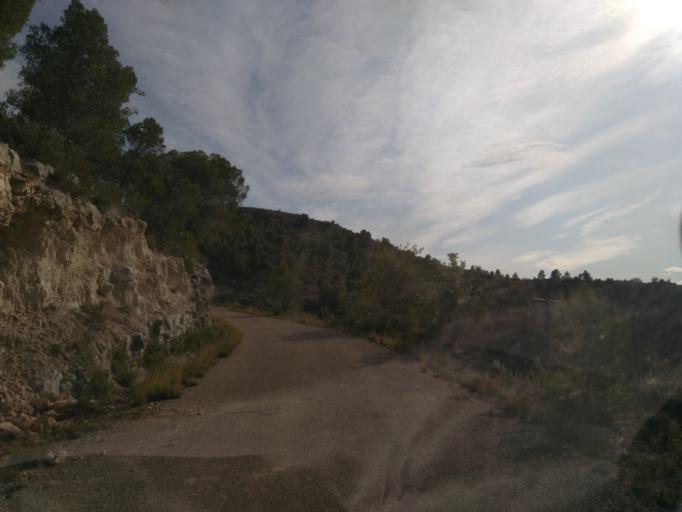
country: ES
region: Valencia
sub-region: Provincia de Valencia
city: Sumacarcer
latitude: 39.1546
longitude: -0.6509
